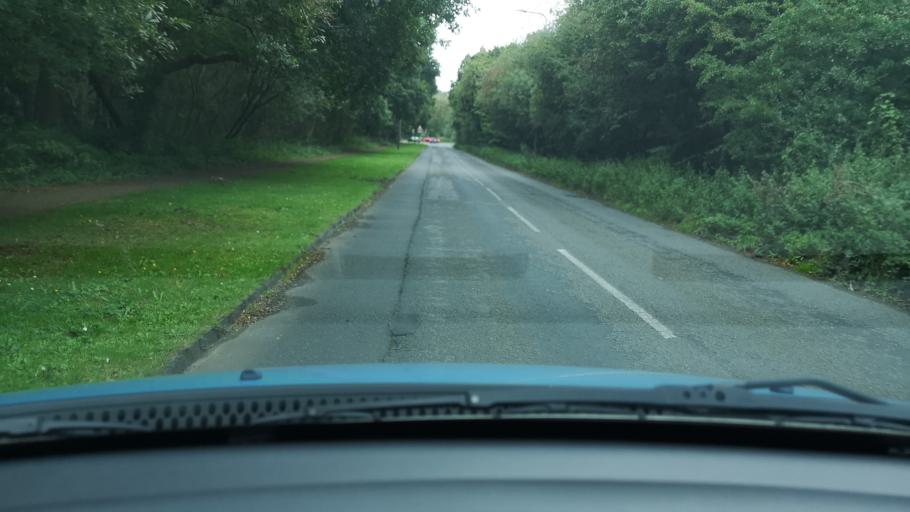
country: GB
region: England
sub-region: North Lincolnshire
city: Scunthorpe
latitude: 53.5843
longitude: -0.6813
